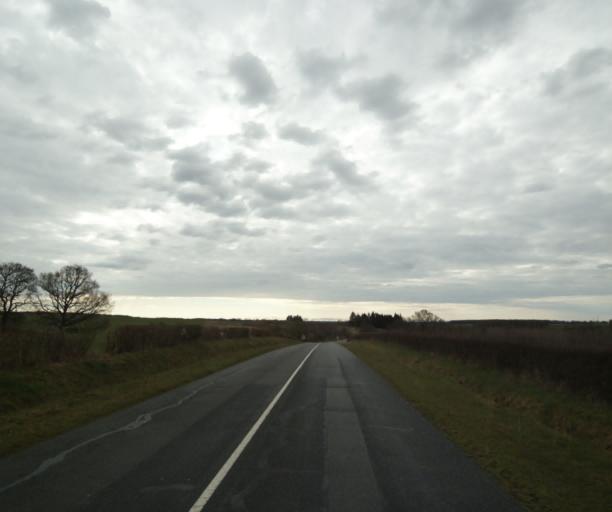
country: FR
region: Auvergne
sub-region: Departement de l'Allier
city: Toulon-sur-Allier
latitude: 46.5031
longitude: 3.3761
